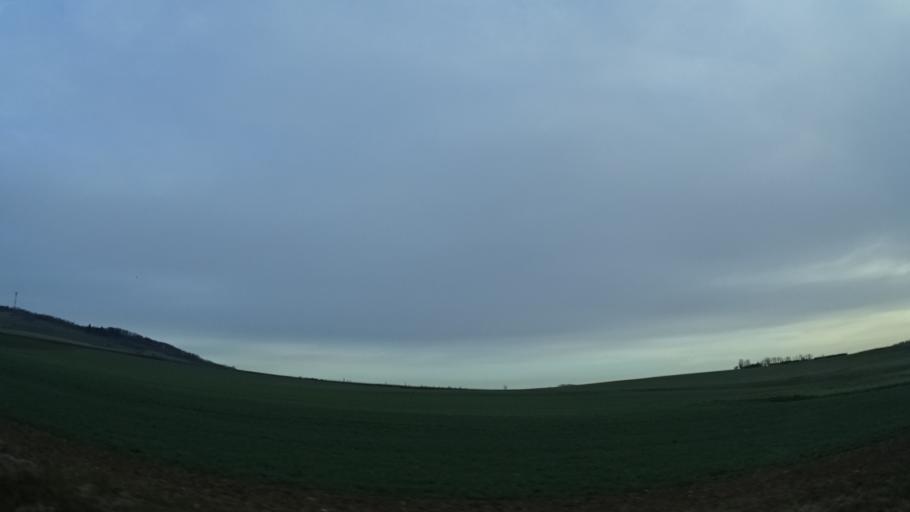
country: DE
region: Rheinland-Pfalz
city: Waldbockelheim
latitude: 49.8176
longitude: 7.7343
